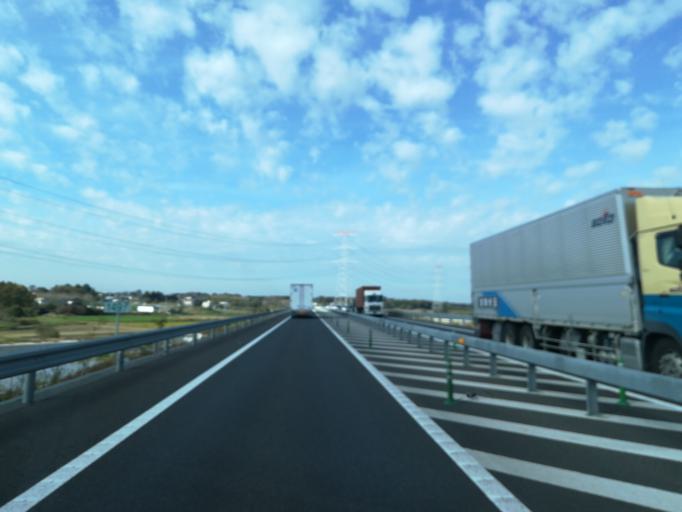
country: JP
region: Ibaraki
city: Mitsukaido
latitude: 36.0589
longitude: 140.0436
